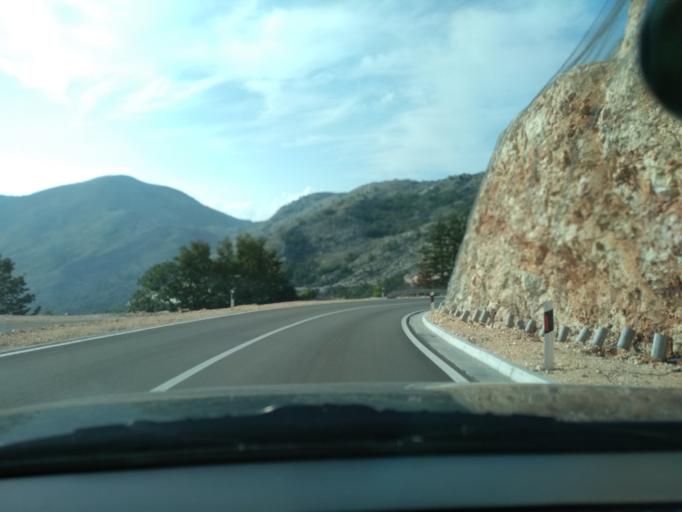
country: ME
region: Kotor
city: Kotor
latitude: 42.4358
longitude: 18.8436
